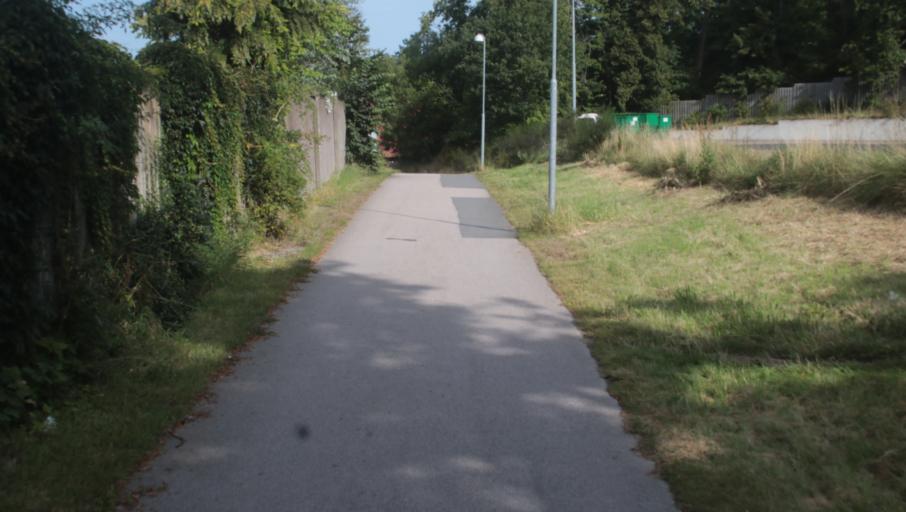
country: SE
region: Blekinge
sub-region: Karlshamns Kommun
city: Karlshamn
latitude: 56.1906
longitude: 14.8476
